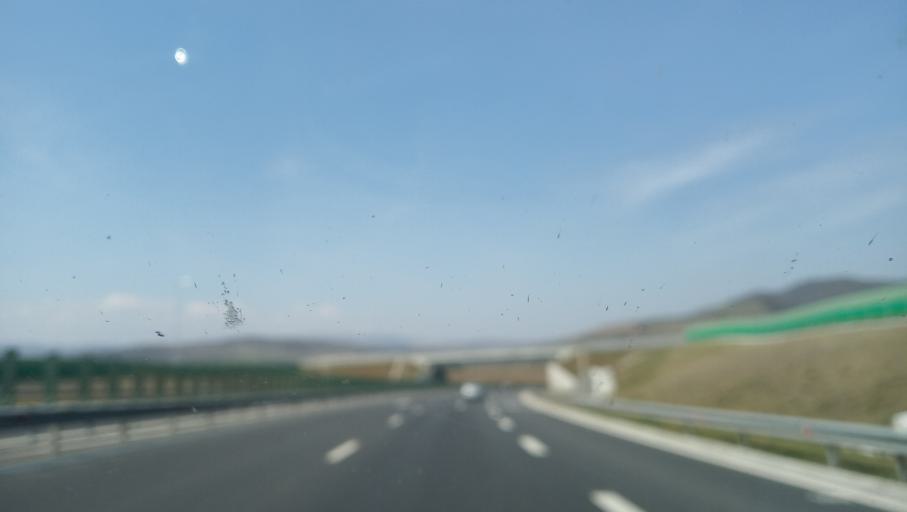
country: RO
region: Alba
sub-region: Comuna Miraslau
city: Miraslau
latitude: 46.3483
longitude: 23.7261
